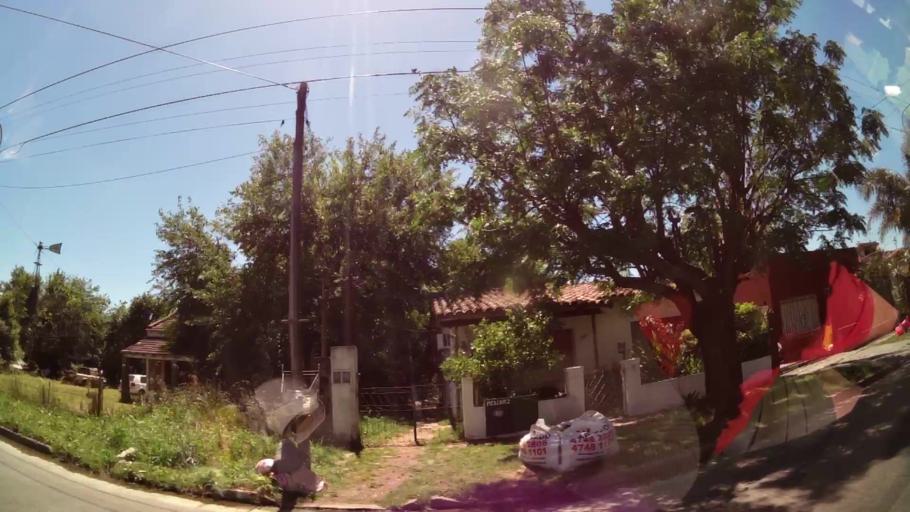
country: AR
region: Buenos Aires
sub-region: Partido de Tigre
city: Tigre
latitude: -34.4972
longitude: -58.6266
